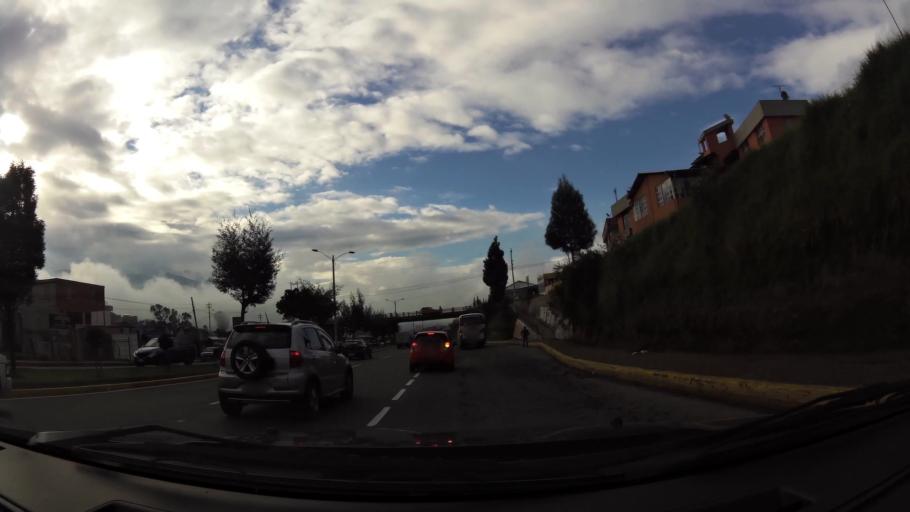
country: EC
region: Pichincha
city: Quito
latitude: -0.2346
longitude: -78.4842
